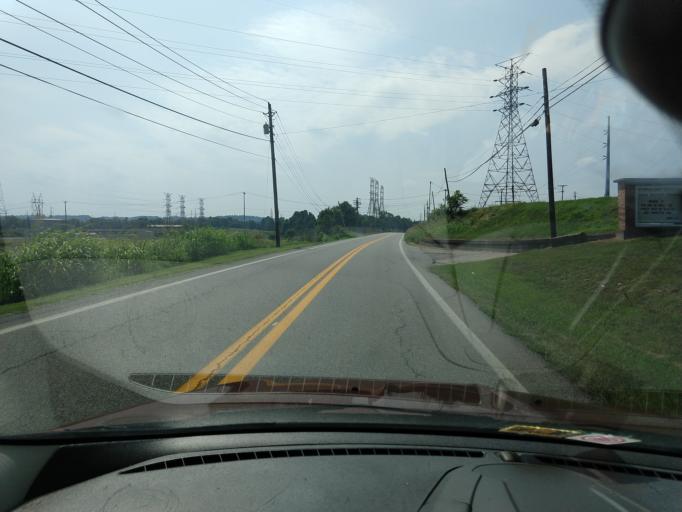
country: US
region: West Virginia
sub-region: Mason County
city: New Haven
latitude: 38.9680
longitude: -81.9299
